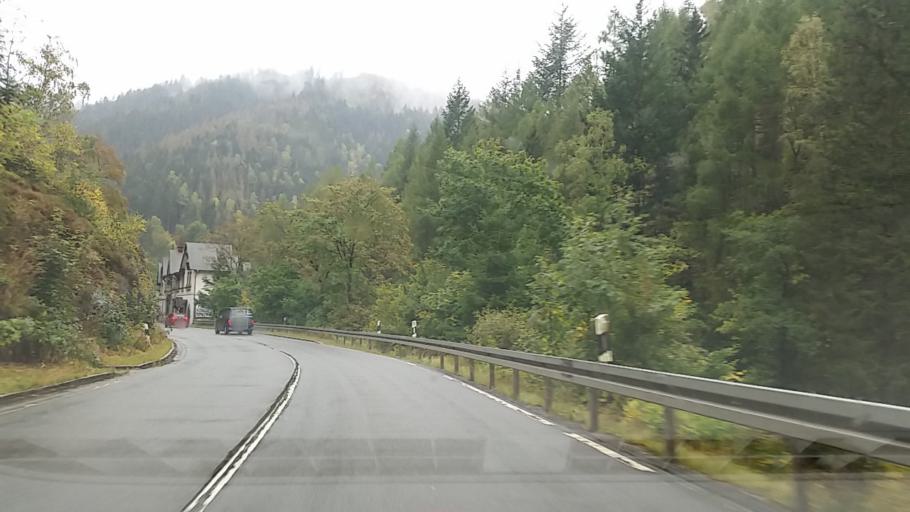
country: DE
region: Lower Saxony
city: Schulenberg im Oberharz
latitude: 51.8606
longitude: 10.4714
